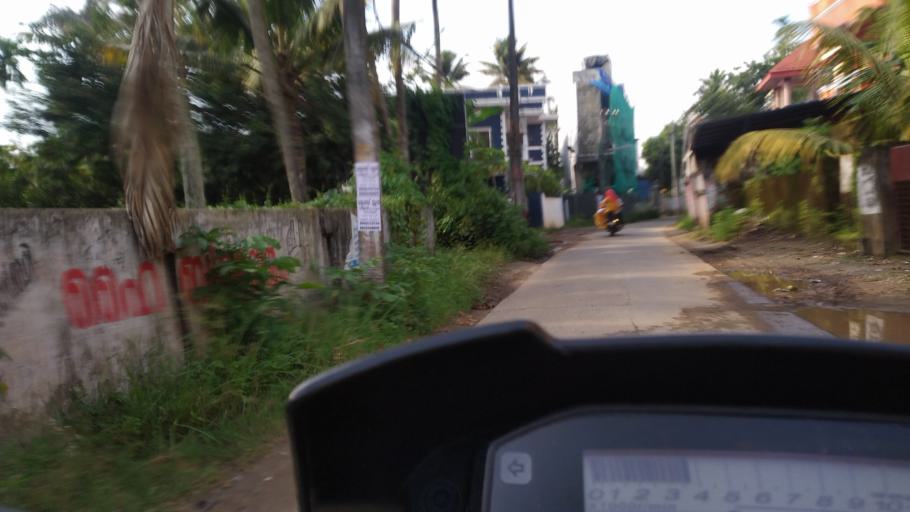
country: IN
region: Kerala
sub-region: Ernakulam
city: Cochin
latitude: 9.9942
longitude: 76.2647
